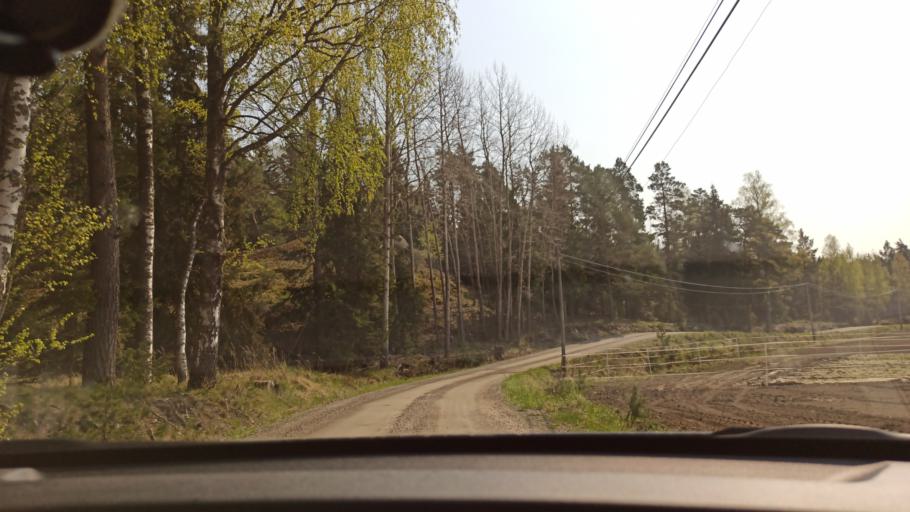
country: FI
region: Uusimaa
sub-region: Helsinki
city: Espoo
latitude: 60.1095
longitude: 24.6317
